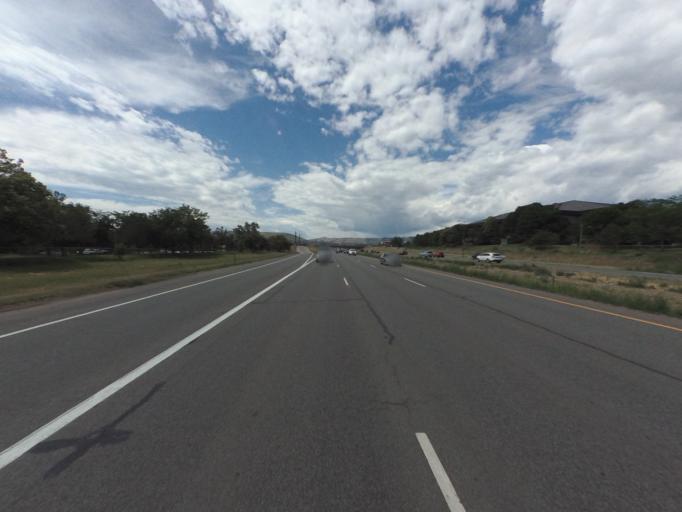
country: US
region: Colorado
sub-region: Jefferson County
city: Applewood
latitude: 39.7421
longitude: -105.1562
